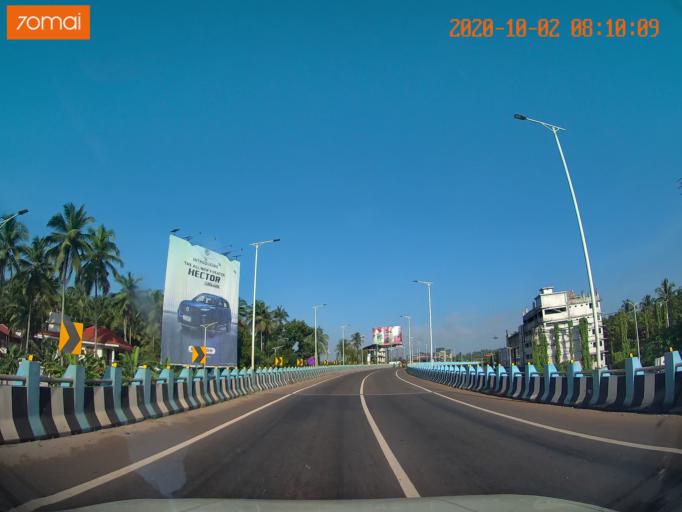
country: IN
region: Kerala
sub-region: Kozhikode
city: Kozhikode
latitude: 11.2636
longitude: 75.8133
